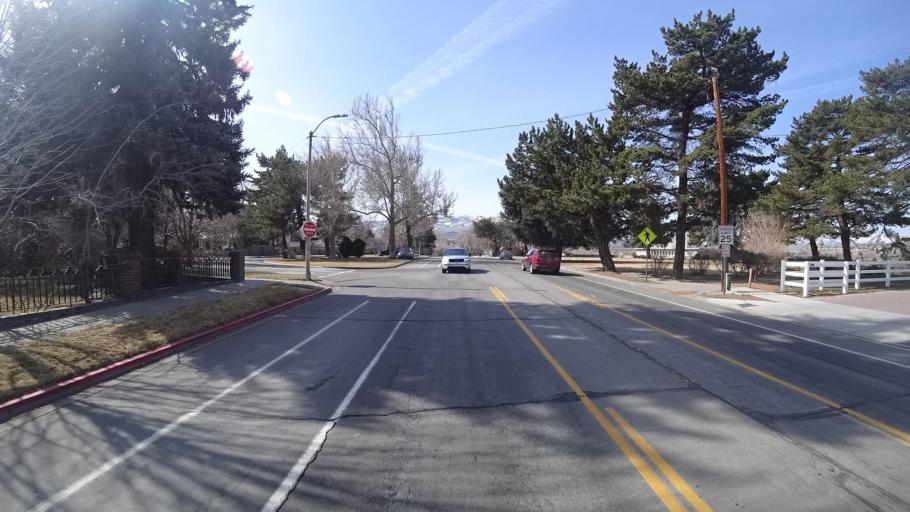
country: US
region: Nevada
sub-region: Washoe County
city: Reno
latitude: 39.5187
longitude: -119.8236
